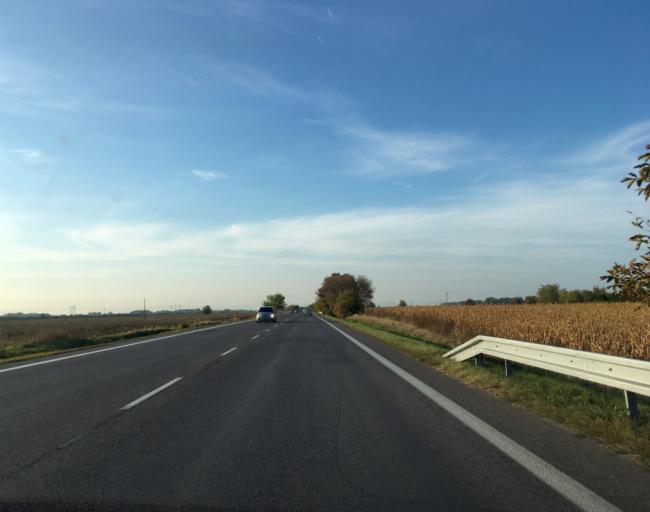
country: SK
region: Nitriansky
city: Sellye
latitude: 48.1676
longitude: 17.8363
